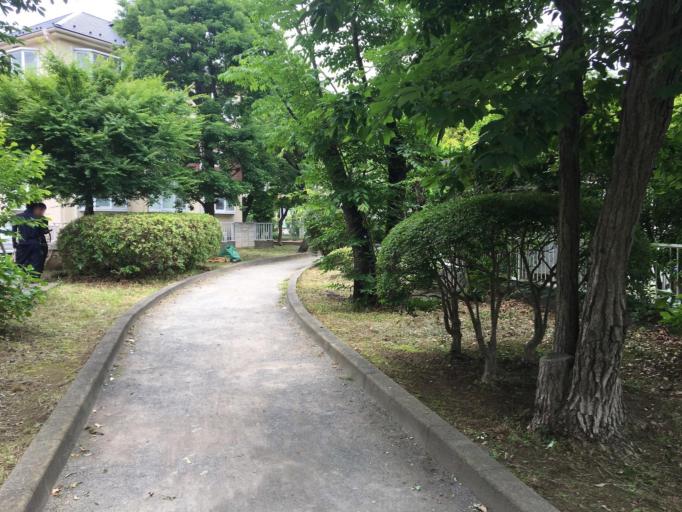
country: JP
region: Tokyo
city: Chofugaoka
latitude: 35.6418
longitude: 139.5808
